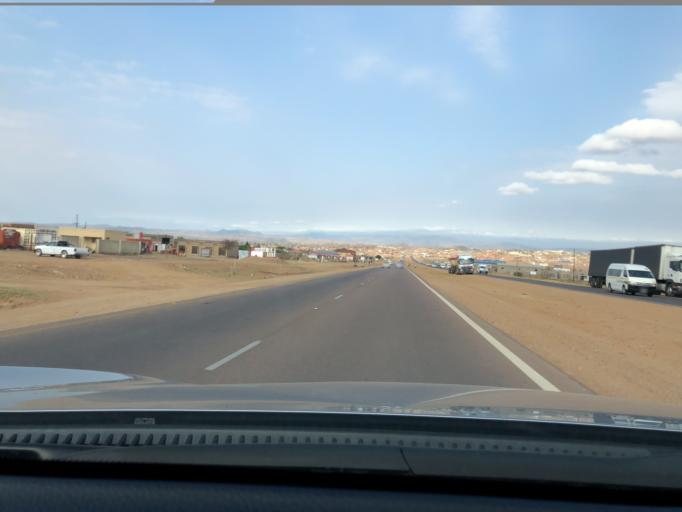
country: ZA
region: Limpopo
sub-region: Capricorn District Municipality
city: Mankoeng
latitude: -23.8887
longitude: 29.6729
